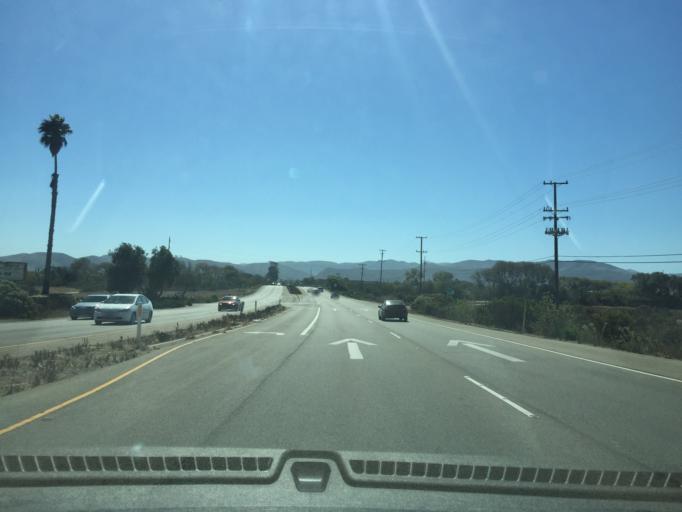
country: US
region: California
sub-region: Santa Barbara County
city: Mission Hills
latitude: 34.6723
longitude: -120.4576
